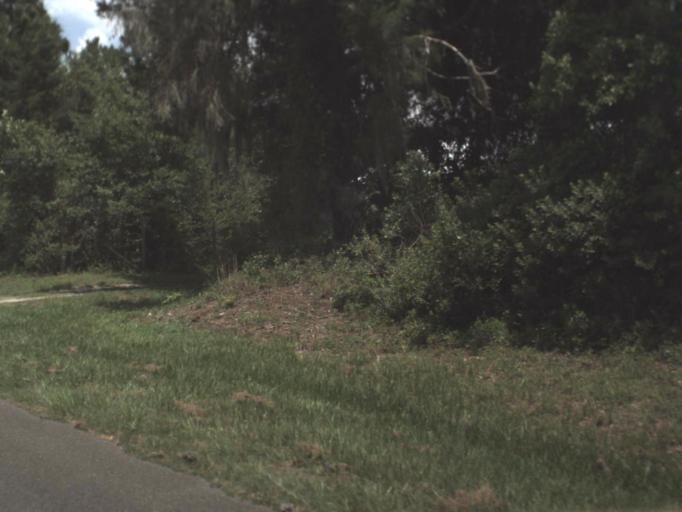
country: US
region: Florida
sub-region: Alachua County
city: Gainesville
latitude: 29.6679
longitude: -82.2473
